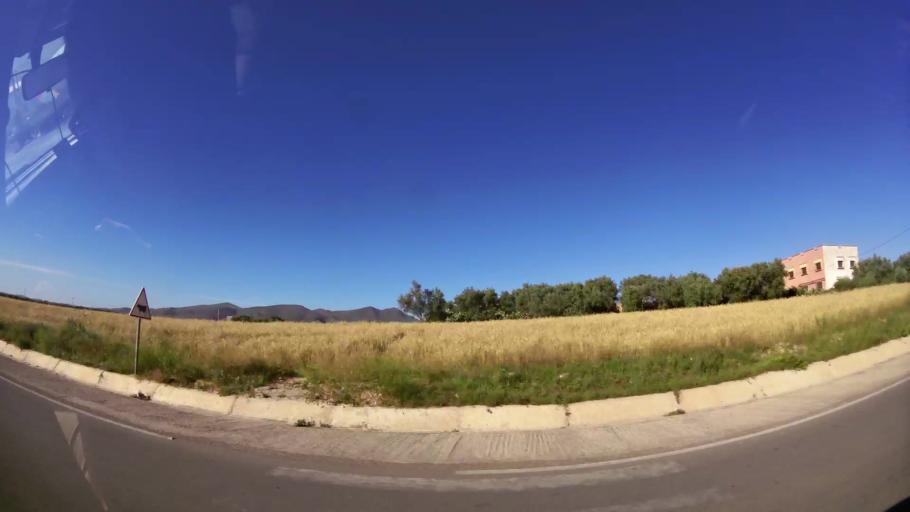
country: MA
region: Oriental
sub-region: Berkane-Taourirt
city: Ahfir
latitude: 34.9648
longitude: -2.1148
